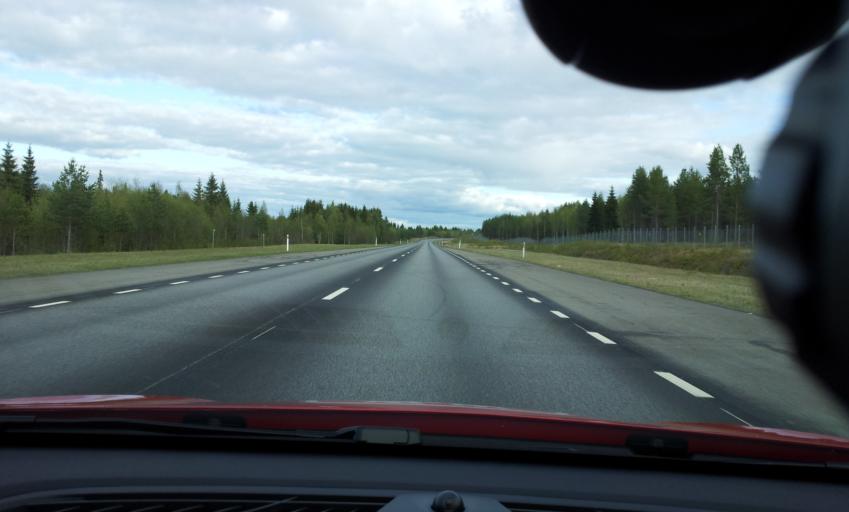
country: SE
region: Jaemtland
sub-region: OEstersunds Kommun
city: Ostersund
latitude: 63.1957
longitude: 14.5169
